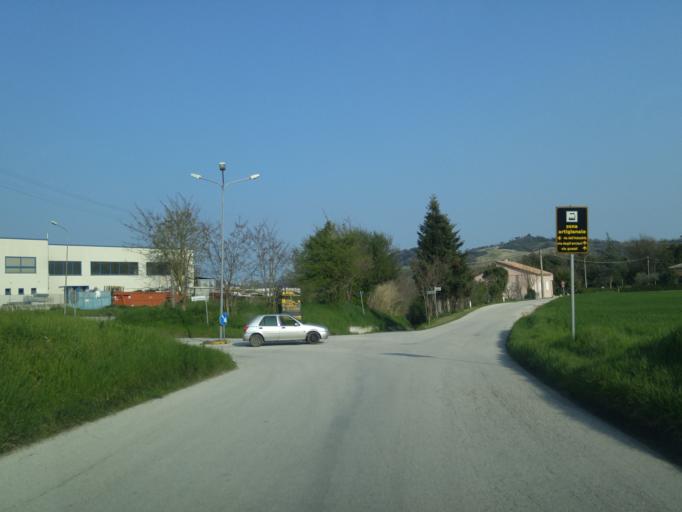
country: IT
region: The Marches
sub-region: Provincia di Pesaro e Urbino
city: Tavernelle
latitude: 43.7330
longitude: 12.9029
